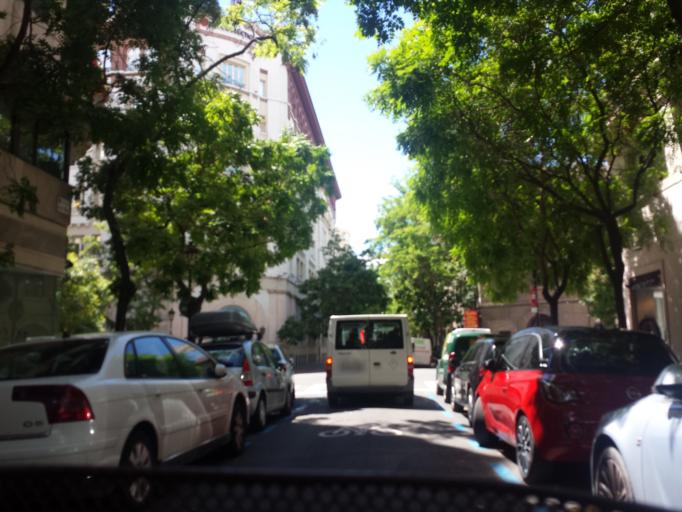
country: ES
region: Aragon
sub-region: Provincia de Zaragoza
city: Zaragoza
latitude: 41.6500
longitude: -0.8811
